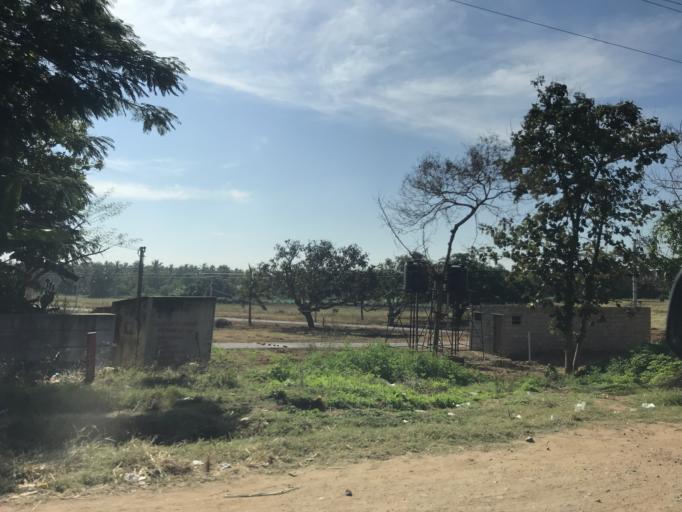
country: IN
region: Karnataka
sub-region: Mysore
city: Mysore
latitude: 12.2028
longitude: 76.5542
